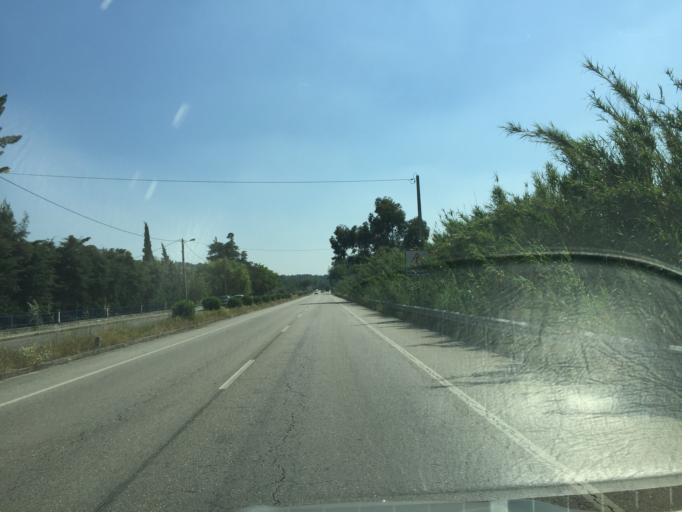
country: PT
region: Santarem
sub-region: Golega
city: Golega
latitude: 39.3960
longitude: -8.4380
